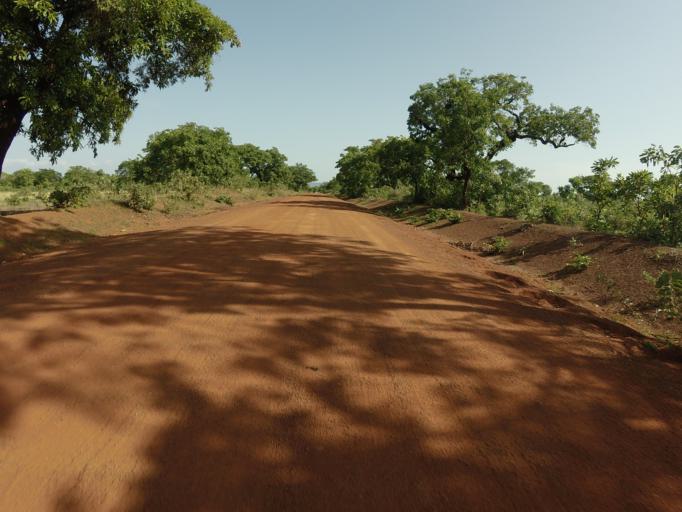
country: GH
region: Upper East
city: Bawku
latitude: 10.7494
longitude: -0.2001
